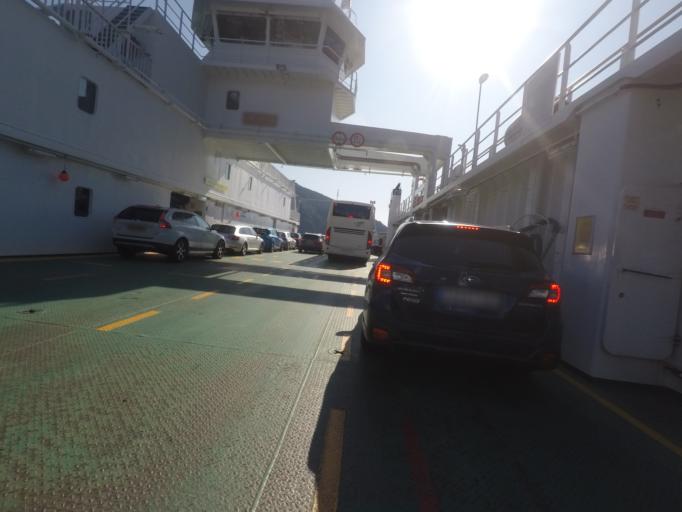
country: NO
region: Sogn og Fjordane
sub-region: Balestrand
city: Balestrand
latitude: 61.2149
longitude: 6.5660
